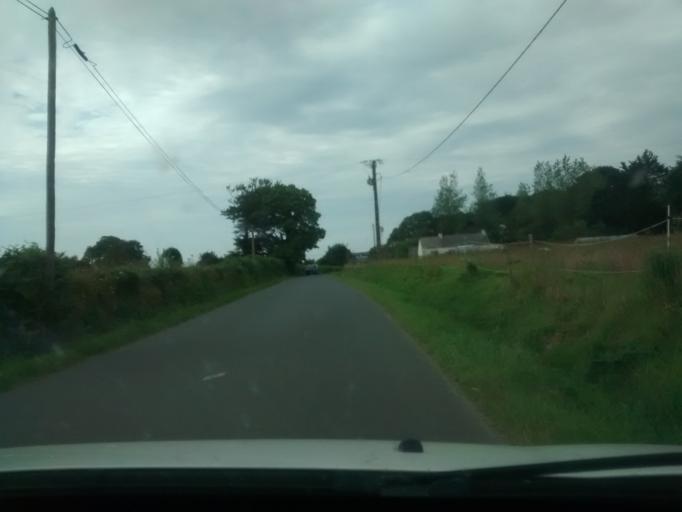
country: FR
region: Brittany
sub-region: Departement des Cotes-d'Armor
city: Trelevern
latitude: 48.7993
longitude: -3.3641
